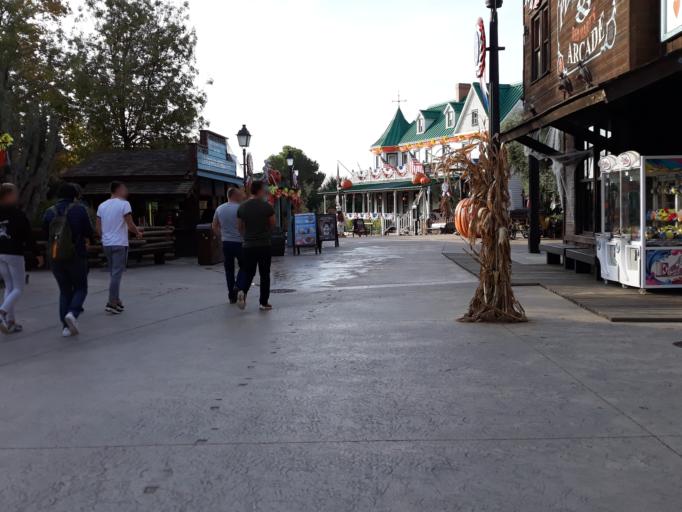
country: ES
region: Catalonia
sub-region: Provincia de Tarragona
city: Salou
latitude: 41.0884
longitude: 1.1559
